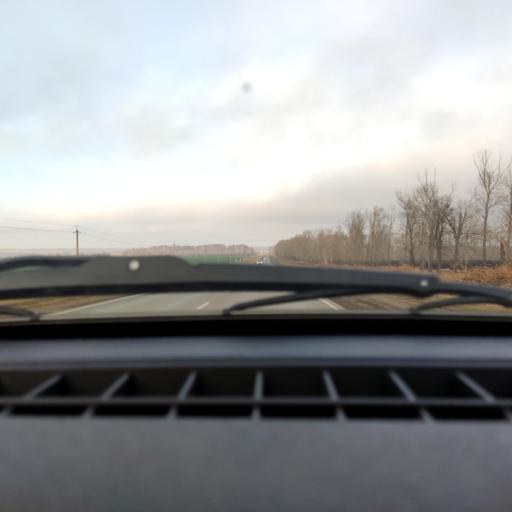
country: RU
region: Bashkortostan
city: Chishmy
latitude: 54.6426
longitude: 55.3800
